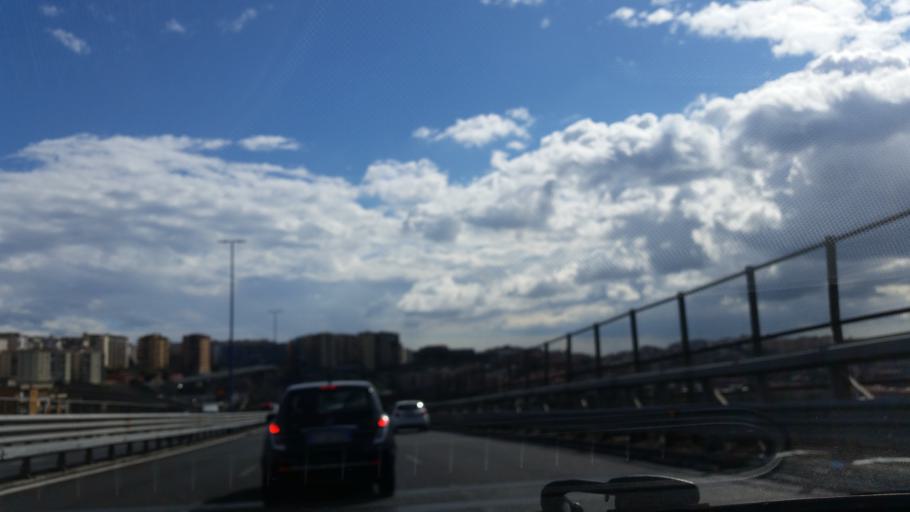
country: IT
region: Campania
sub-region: Provincia di Napoli
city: Napoli
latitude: 40.8492
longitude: 14.2149
